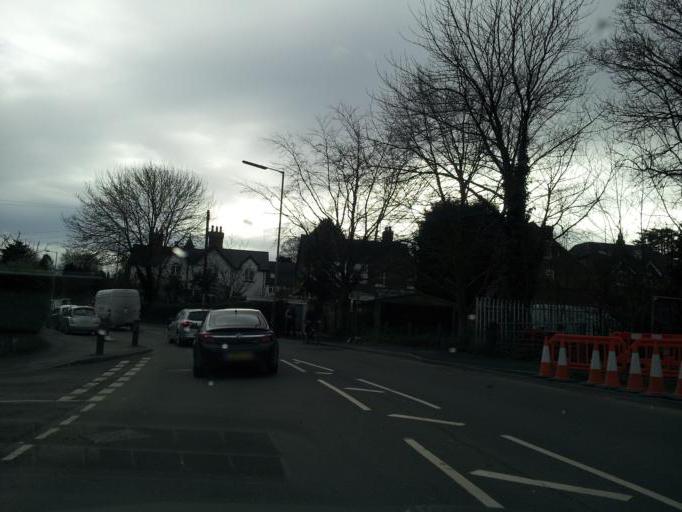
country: GB
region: England
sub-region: Staffordshire
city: Stafford
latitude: 52.7972
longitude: -2.1176
